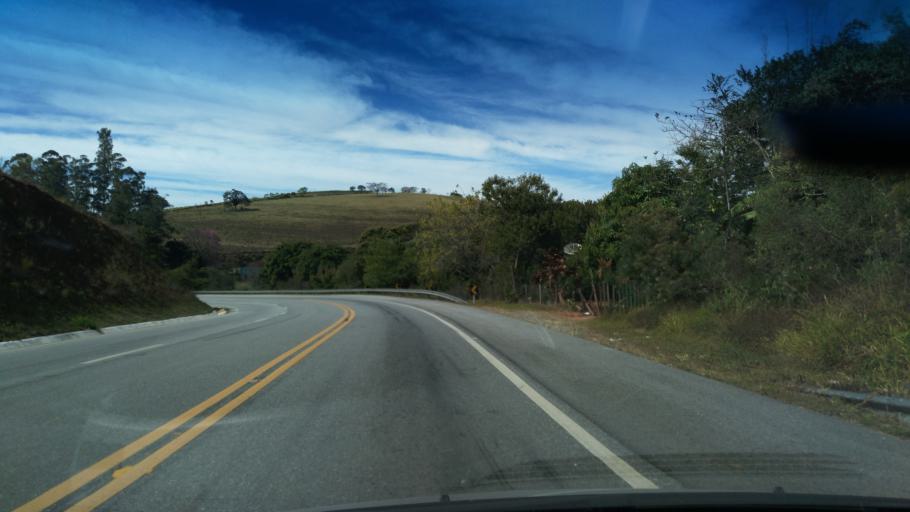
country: BR
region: Minas Gerais
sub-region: Borda Da Mata
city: Borda da Mata
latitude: -22.1412
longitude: -46.1441
